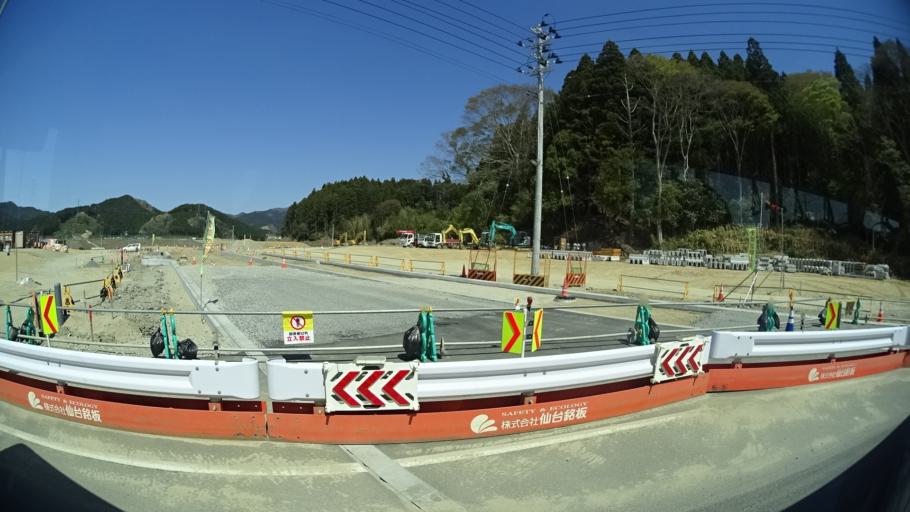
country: JP
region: Iwate
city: Ofunato
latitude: 39.0178
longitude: 141.6276
